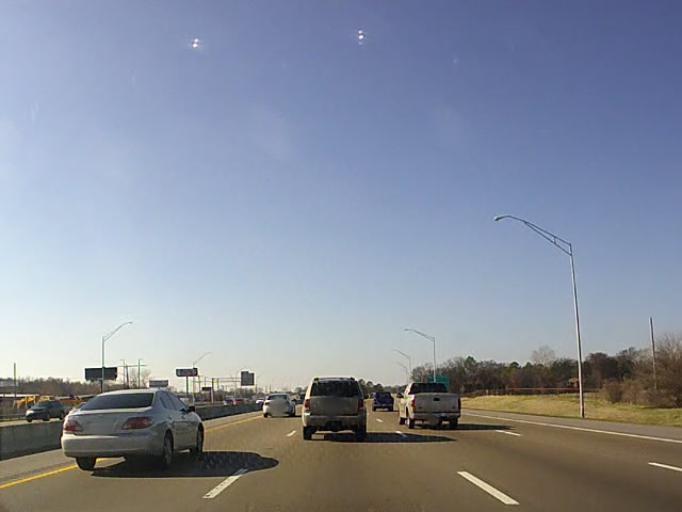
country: US
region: Tennessee
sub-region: Shelby County
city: New South Memphis
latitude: 35.0765
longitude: -89.9771
